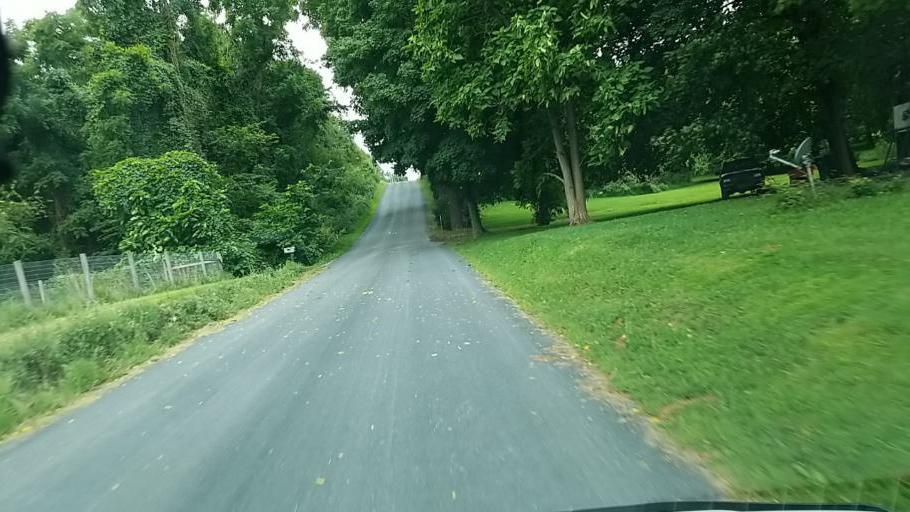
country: US
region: Pennsylvania
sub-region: Dauphin County
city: Elizabethville
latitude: 40.5755
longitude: -76.8325
